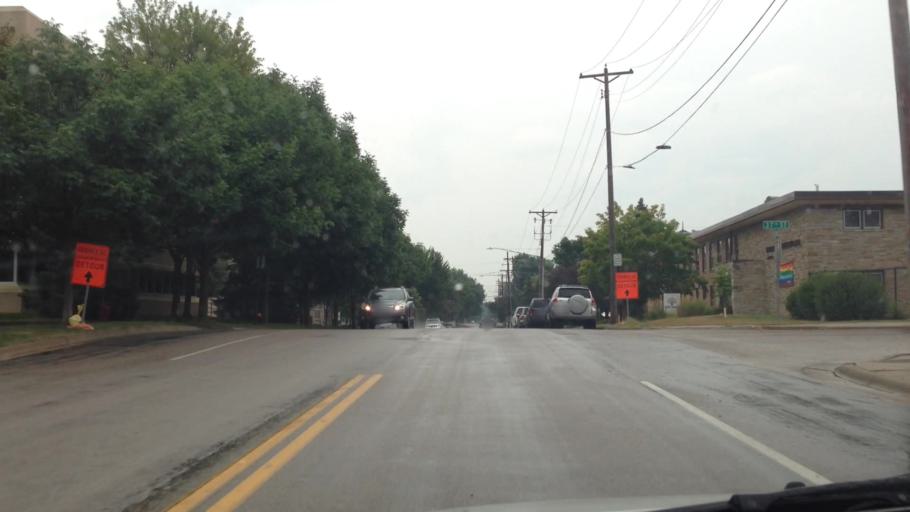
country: US
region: Minnesota
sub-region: Hennepin County
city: Saint Louis Park
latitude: 44.9370
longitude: -93.3562
